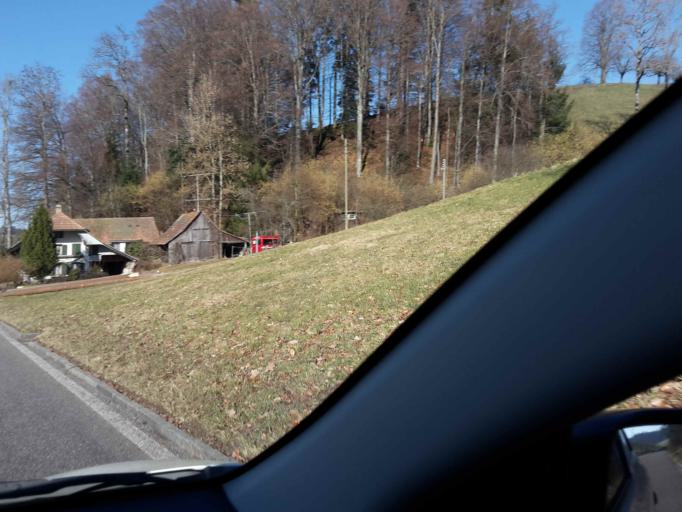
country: CH
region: Bern
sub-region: Emmental District
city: Durrenroth
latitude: 47.1057
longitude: 7.7760
